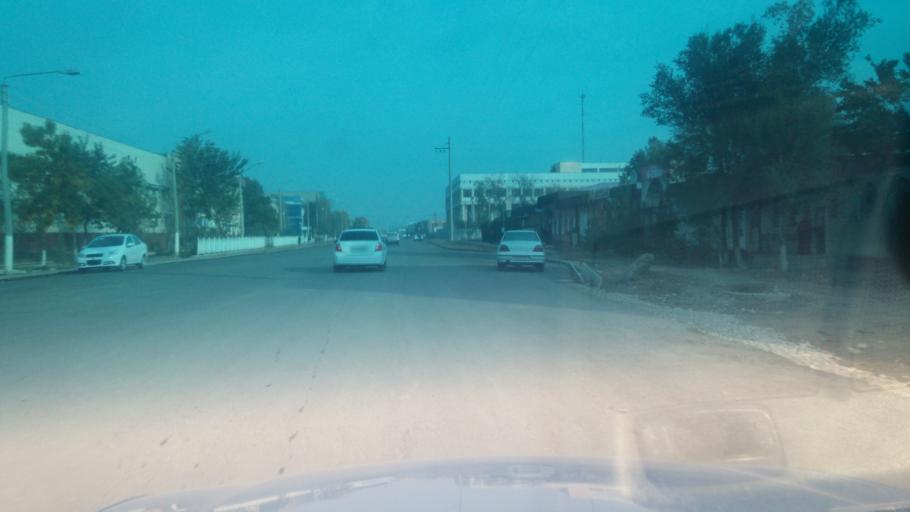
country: UZ
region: Sirdaryo
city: Guliston
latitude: 40.4953
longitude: 68.7738
